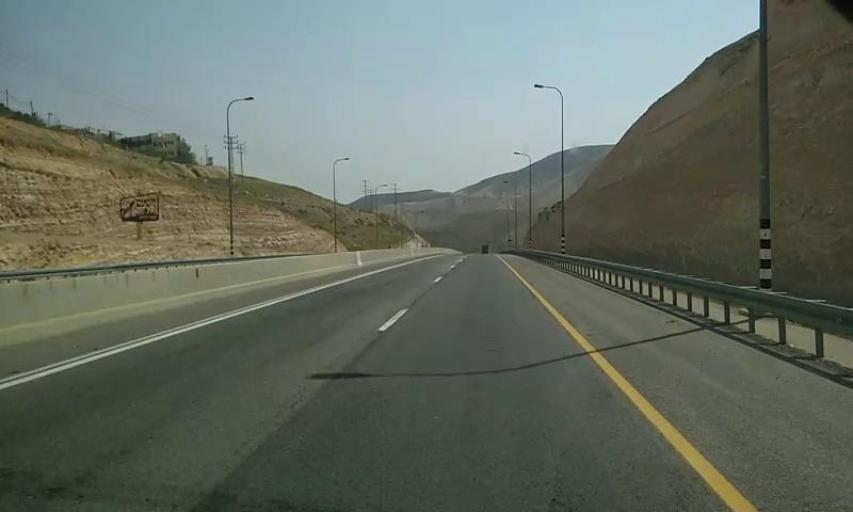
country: PS
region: West Bank
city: Jericho
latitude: 31.8146
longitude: 35.3899
